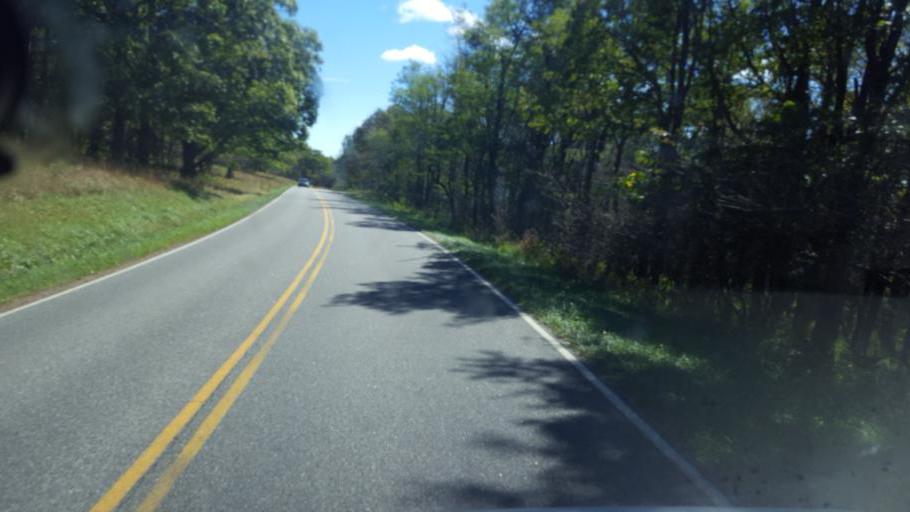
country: US
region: Virginia
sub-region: Page County
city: Stanley
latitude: 38.5109
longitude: -78.4446
